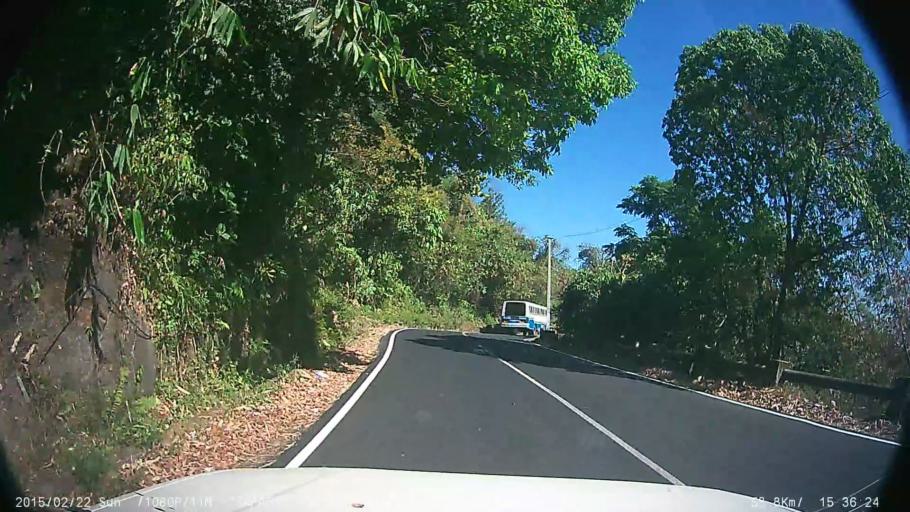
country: IN
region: Kerala
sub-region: Kottayam
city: Erattupetta
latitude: 9.5627
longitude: 76.9779
